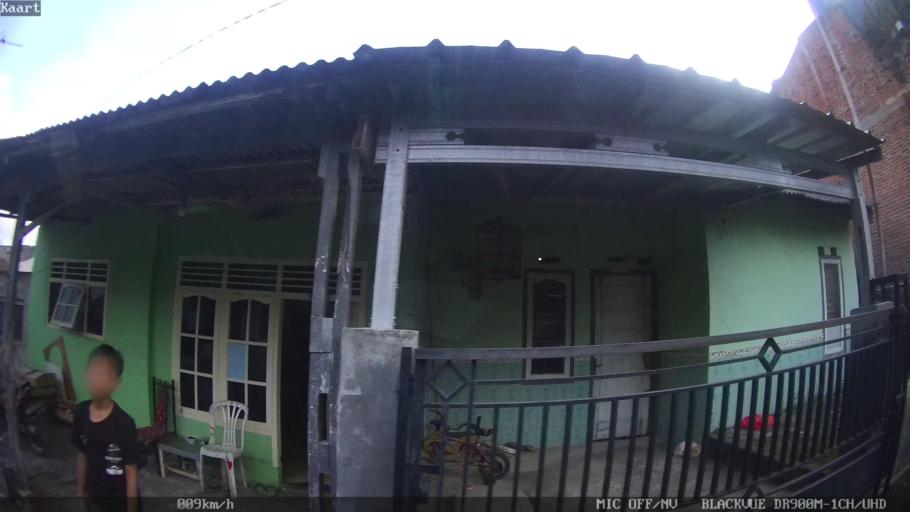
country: ID
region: Lampung
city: Kedaton
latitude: -5.4027
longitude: 105.2948
